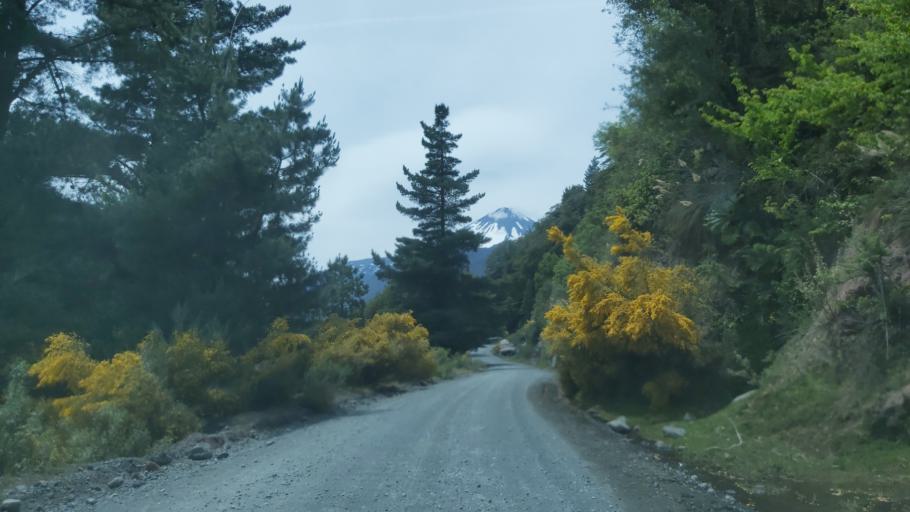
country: AR
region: Neuquen
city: Las Ovejas
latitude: -37.3969
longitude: -71.4507
